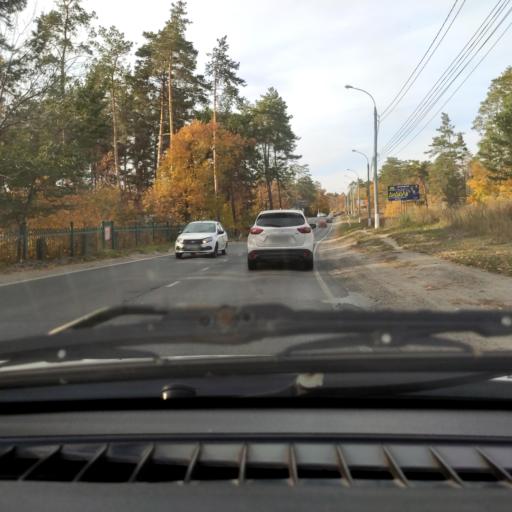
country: RU
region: Samara
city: Tol'yatti
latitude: 53.4830
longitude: 49.3184
